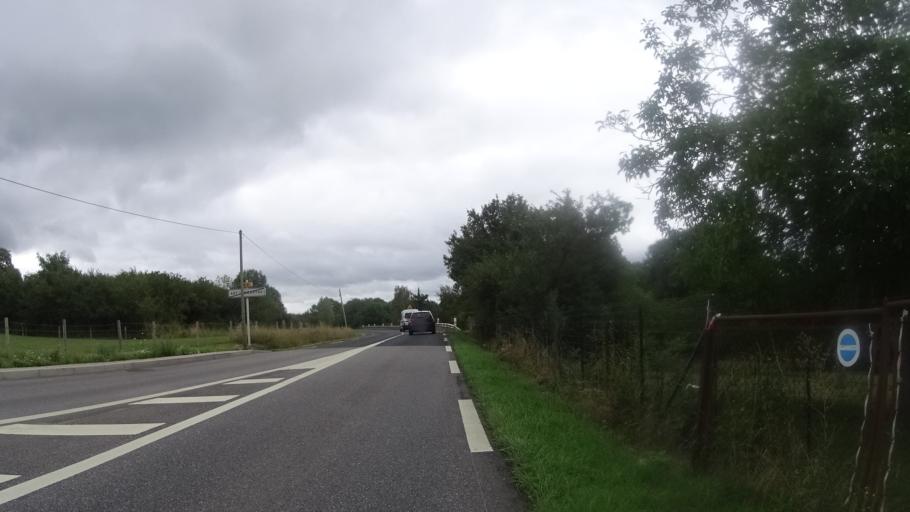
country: FR
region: Lorraine
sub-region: Departement de Meurthe-et-Moselle
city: Art-sur-Meurthe
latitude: 48.6516
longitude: 6.2704
